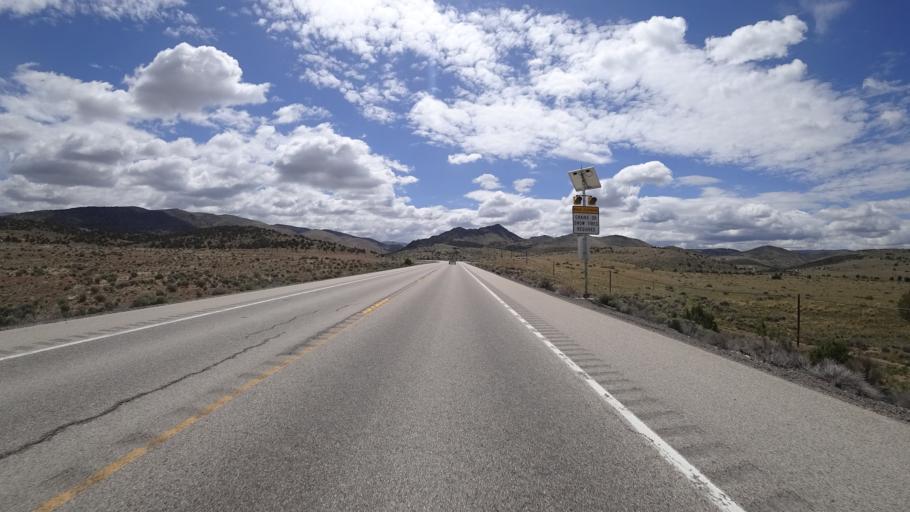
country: US
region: Nevada
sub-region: Douglas County
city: Gardnerville Ranchos
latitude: 38.8575
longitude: -119.6661
